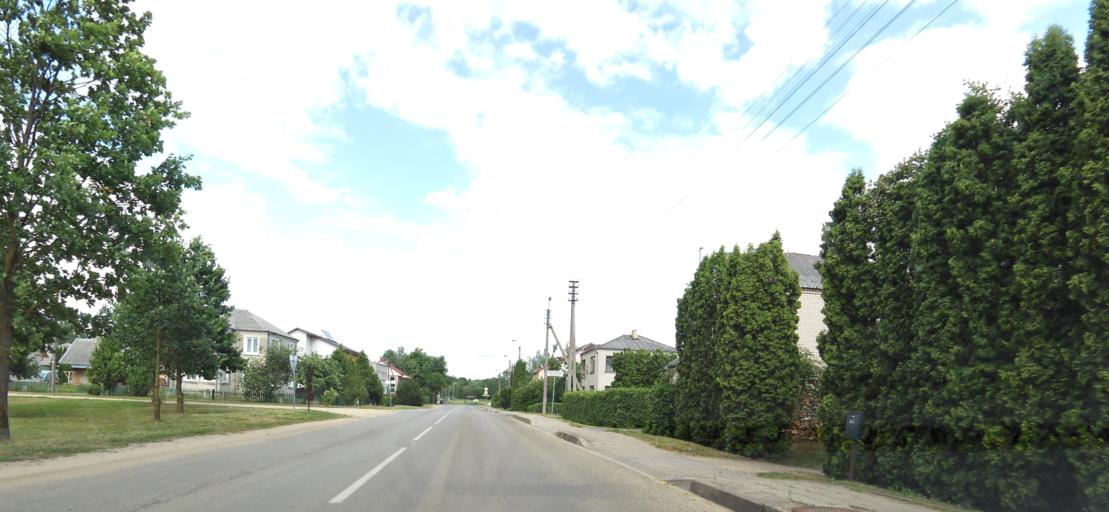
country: LT
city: Kupiskis
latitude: 55.8428
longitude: 24.9866
